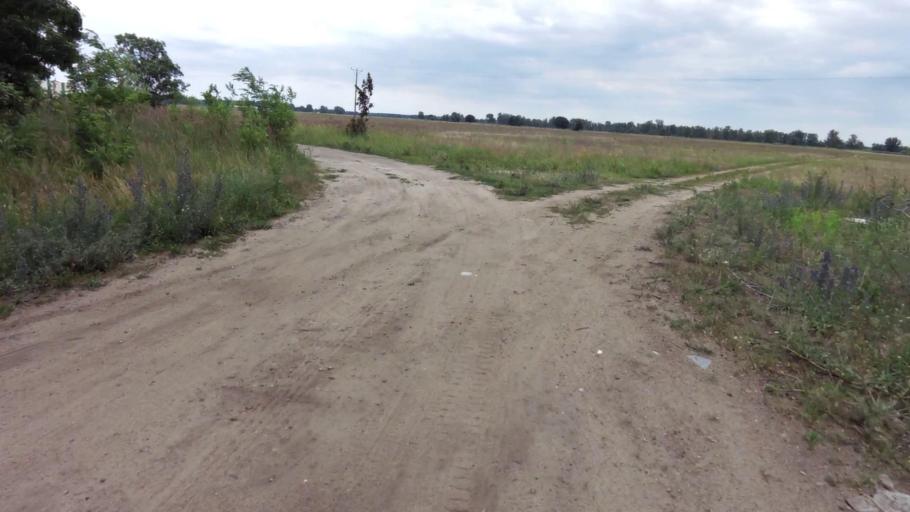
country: PL
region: Lubusz
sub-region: Powiat gorzowski
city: Kostrzyn nad Odra
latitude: 52.6138
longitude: 14.6052
